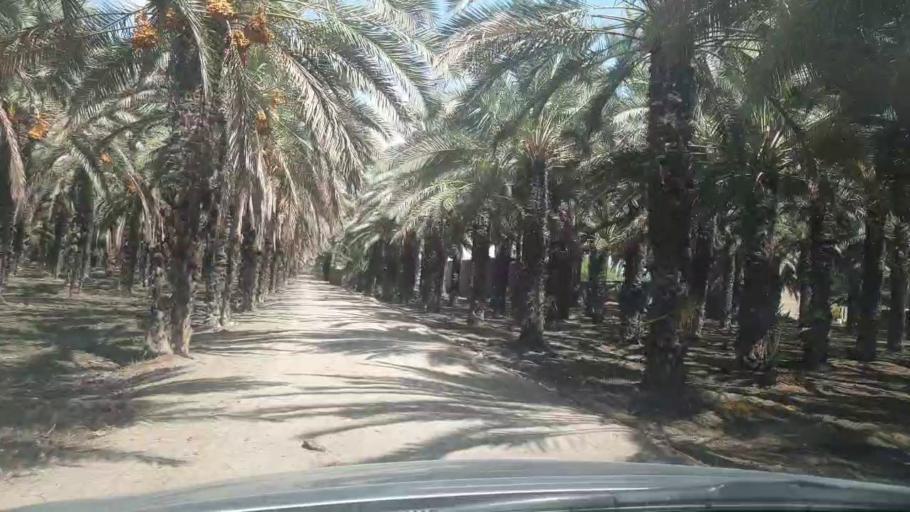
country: PK
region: Sindh
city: Khairpur
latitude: 27.5493
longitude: 68.7981
